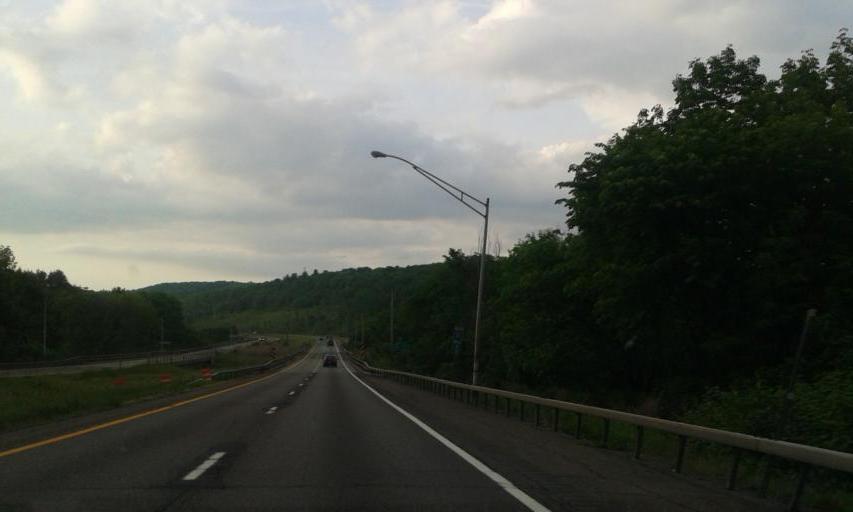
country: US
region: New York
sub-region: Broome County
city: Port Dickinson
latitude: 42.1618
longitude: -75.8966
